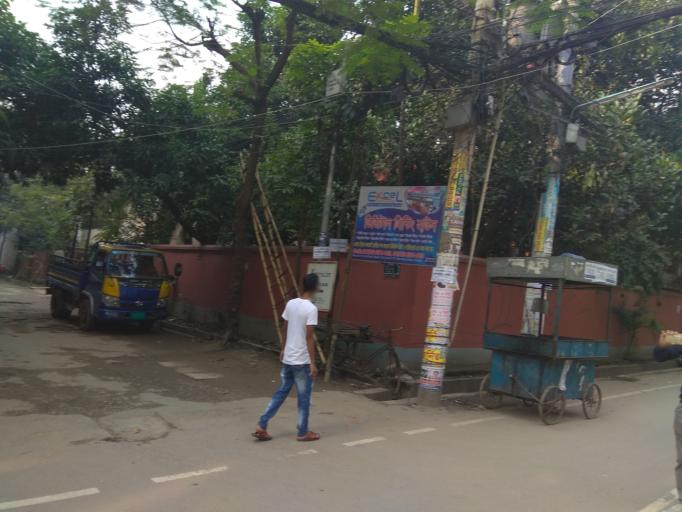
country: BD
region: Dhaka
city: Tungi
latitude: 23.8684
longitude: 90.3991
